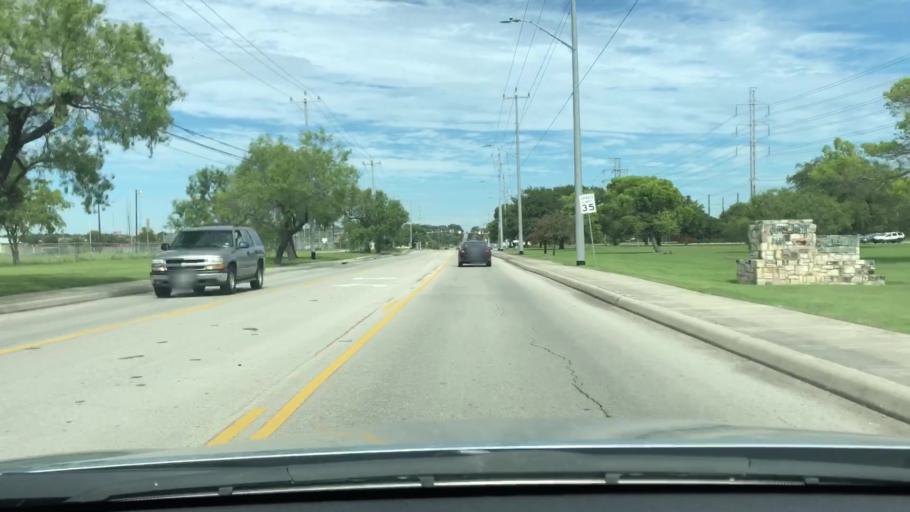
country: US
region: Texas
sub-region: Bexar County
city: Olmos Park
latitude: 29.4855
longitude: -98.4917
